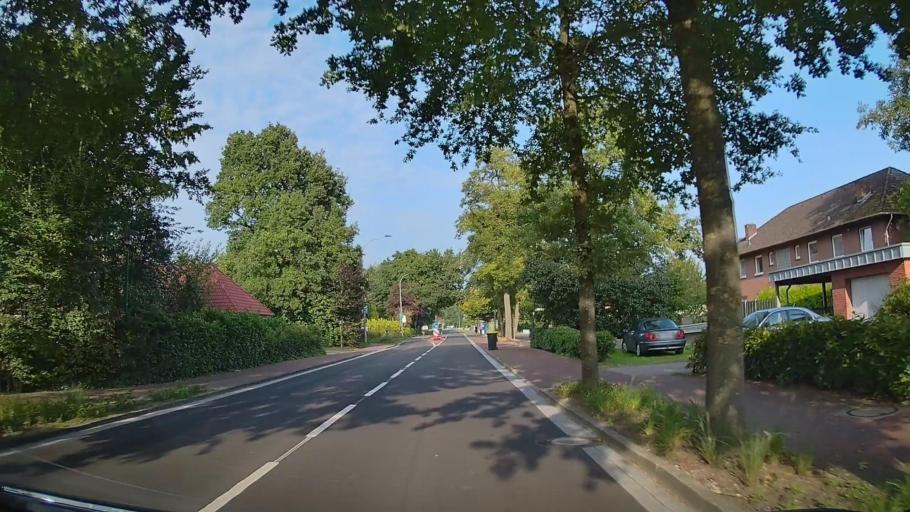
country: DE
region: Lower Saxony
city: Barssel
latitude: 53.1710
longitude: 7.7492
